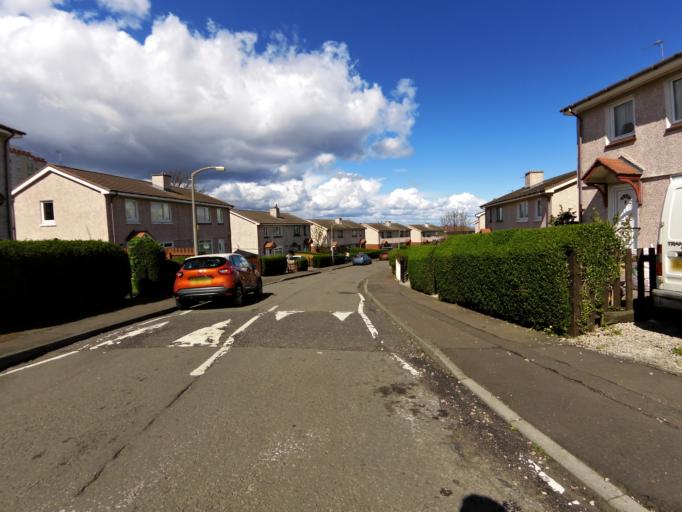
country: GB
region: Scotland
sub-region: Midlothian
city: Loanhead
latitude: 55.9153
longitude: -3.1367
